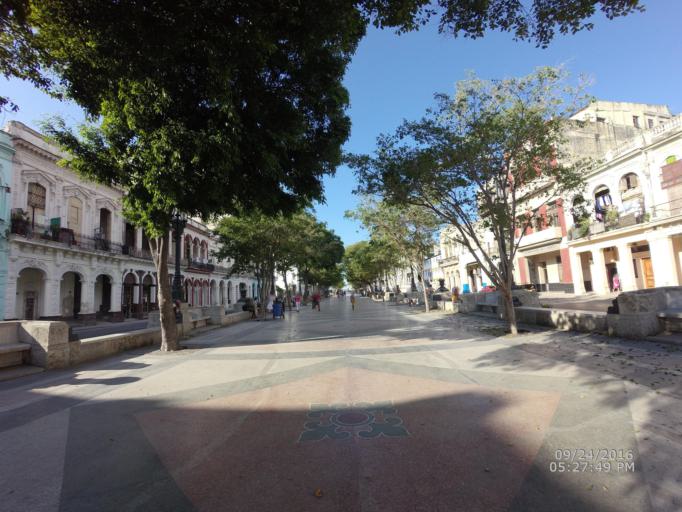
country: CU
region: La Habana
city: Centro Habana
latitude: 23.1424
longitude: -82.3587
